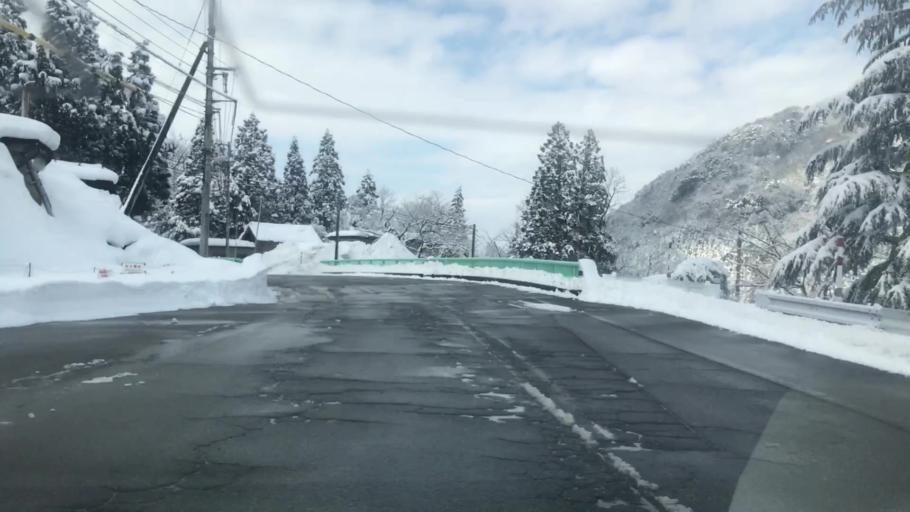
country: JP
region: Toyama
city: Kamiichi
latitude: 36.5715
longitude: 137.3477
